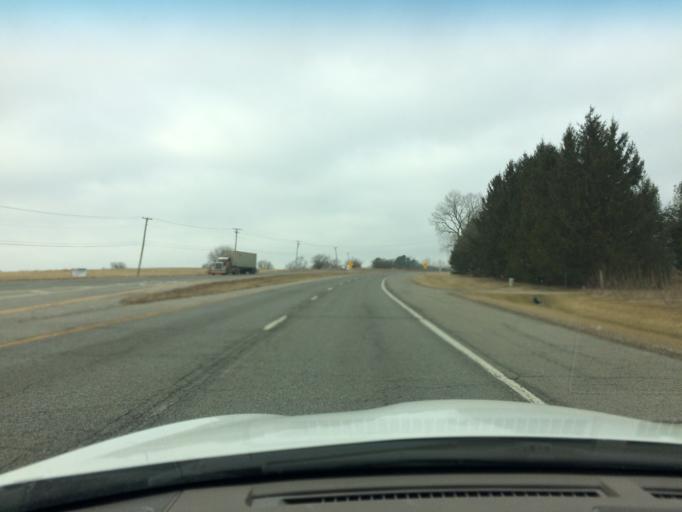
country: US
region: Illinois
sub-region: Kane County
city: Sugar Grove
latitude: 41.7902
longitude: -88.4579
